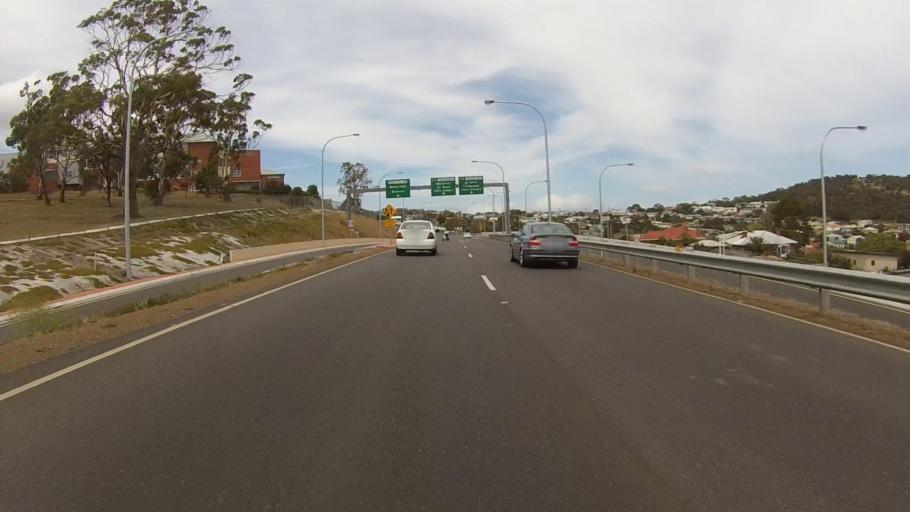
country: AU
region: Tasmania
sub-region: Clarence
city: Lindisfarne
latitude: -42.8620
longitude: 147.3563
